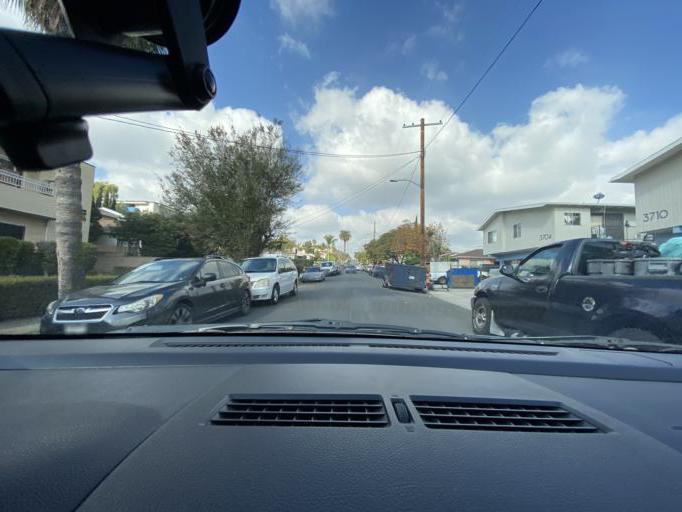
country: US
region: California
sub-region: Los Angeles County
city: Culver City
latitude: 34.0154
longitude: -118.4172
